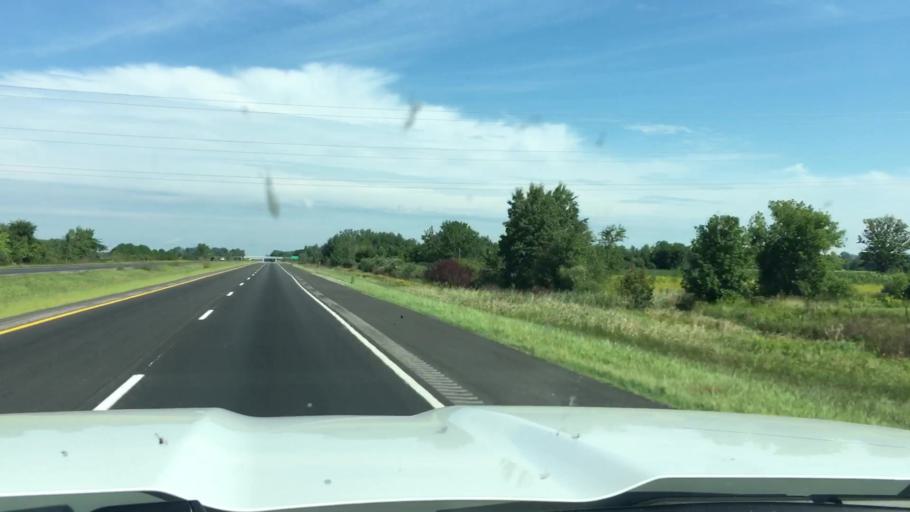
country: US
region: Michigan
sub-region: Saginaw County
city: Freeland
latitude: 43.5558
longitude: -84.1386
